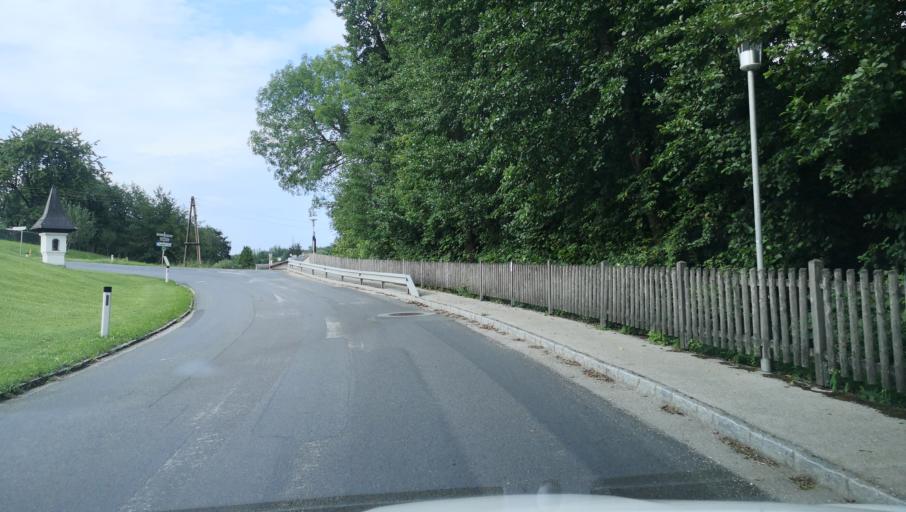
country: AT
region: Lower Austria
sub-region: Politischer Bezirk Amstetten
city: Sankt Georgen am Ybbsfelde
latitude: 48.1372
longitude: 14.9217
